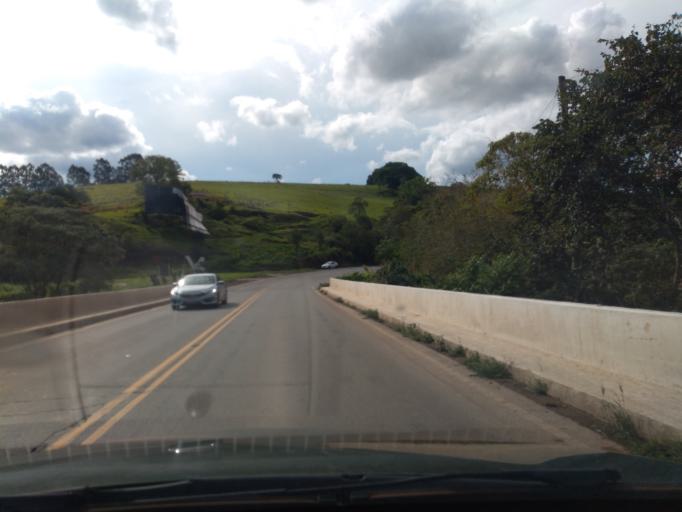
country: BR
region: Minas Gerais
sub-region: Varginha
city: Varginha
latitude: -21.6115
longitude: -45.4309
